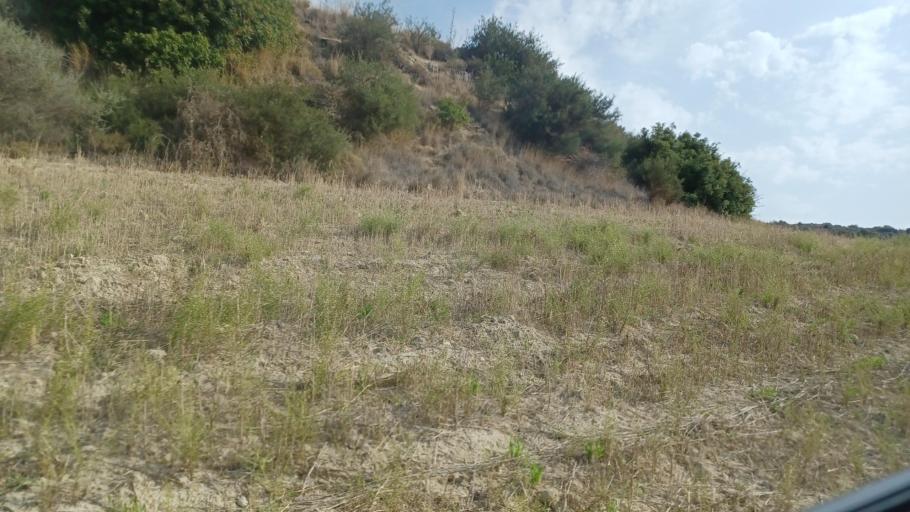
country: CY
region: Pafos
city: Polis
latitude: 34.9717
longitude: 32.4557
